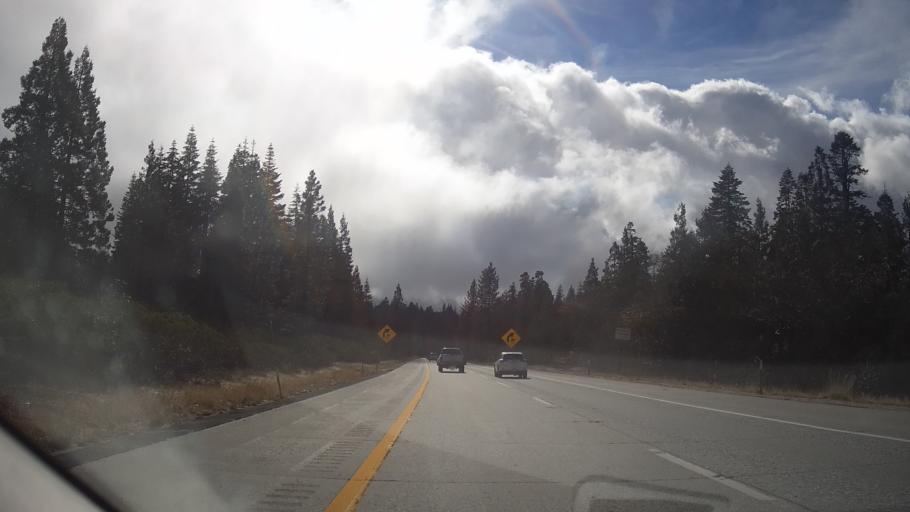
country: US
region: California
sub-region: Placer County
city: Foresthill
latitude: 39.2754
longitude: -120.7164
